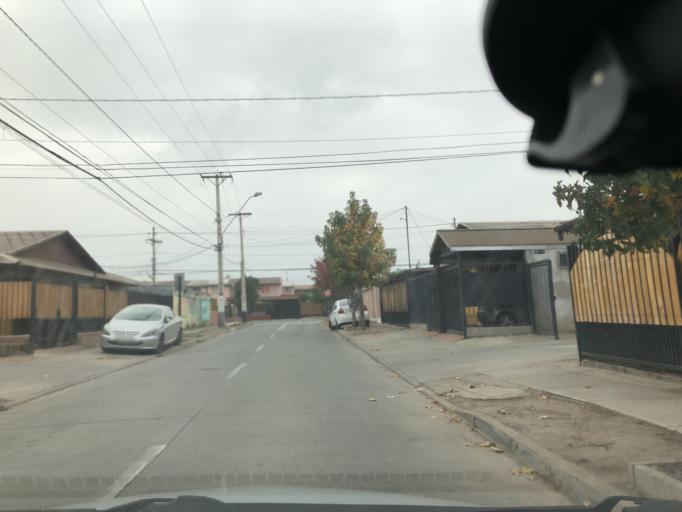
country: CL
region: Santiago Metropolitan
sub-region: Provincia de Santiago
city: La Pintana
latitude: -33.5773
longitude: -70.6049
